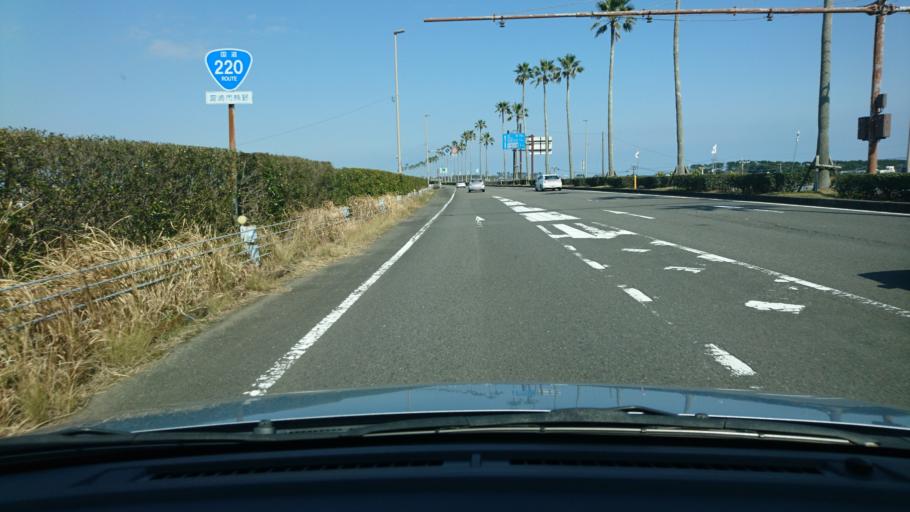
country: JP
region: Miyazaki
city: Miyazaki-shi
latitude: 31.8310
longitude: 131.4431
